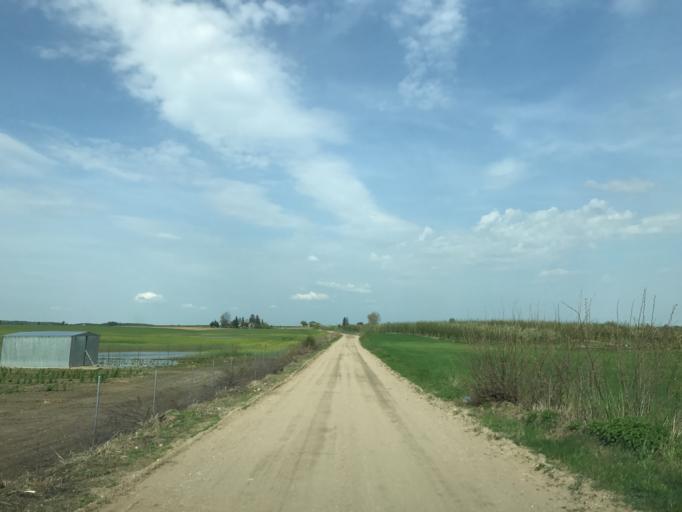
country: PL
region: Warmian-Masurian Voivodeship
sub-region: Powiat dzialdowski
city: Rybno
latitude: 53.4006
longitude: 19.8600
